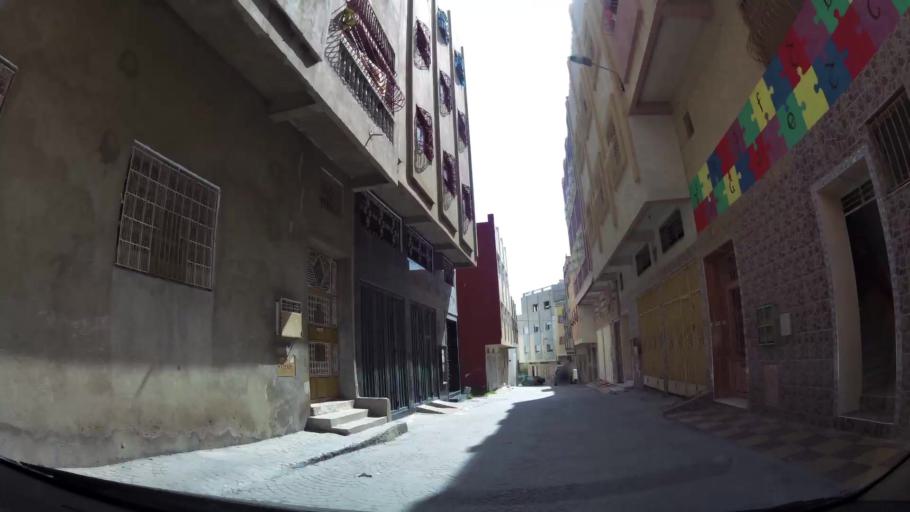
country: MA
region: Tanger-Tetouan
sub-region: Tanger-Assilah
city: Tangier
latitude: 35.7304
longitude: -5.8063
